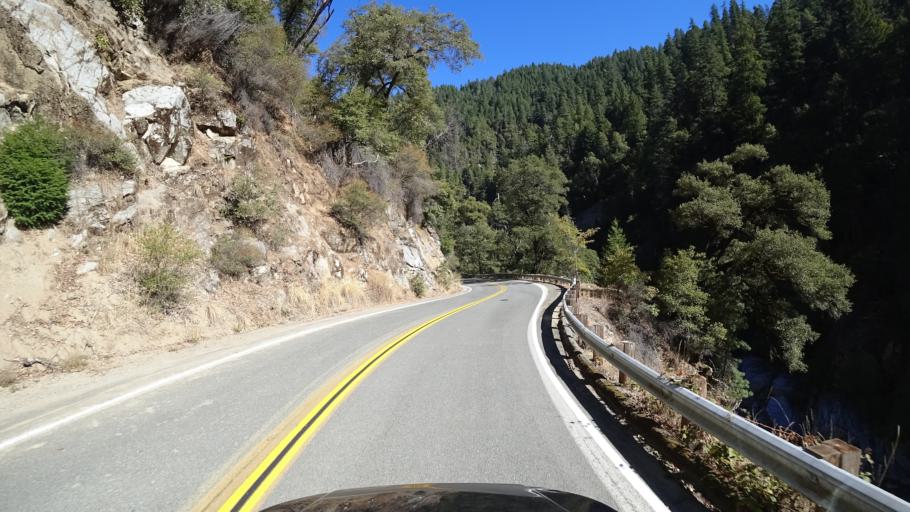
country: US
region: California
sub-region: Siskiyou County
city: Happy Camp
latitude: 41.3444
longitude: -123.4040
